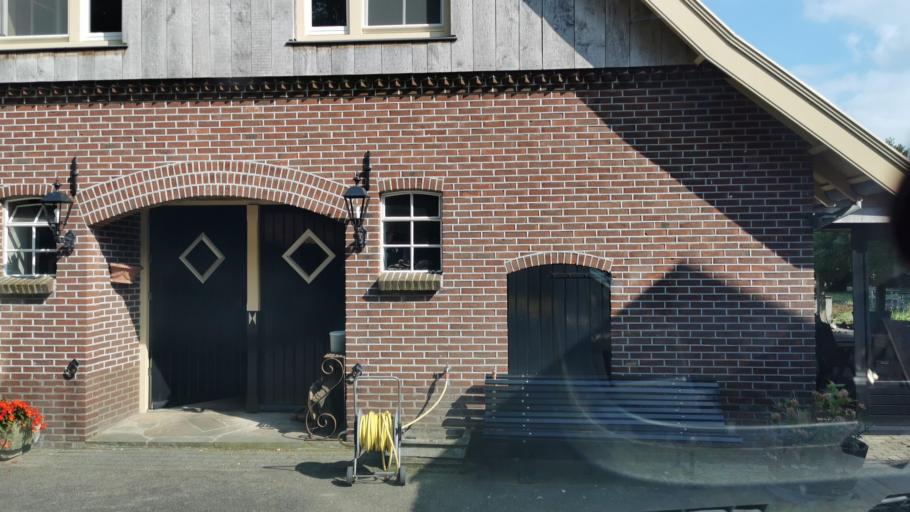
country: NL
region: Overijssel
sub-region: Gemeente Borne
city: Borne
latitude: 52.3249
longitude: 6.8013
